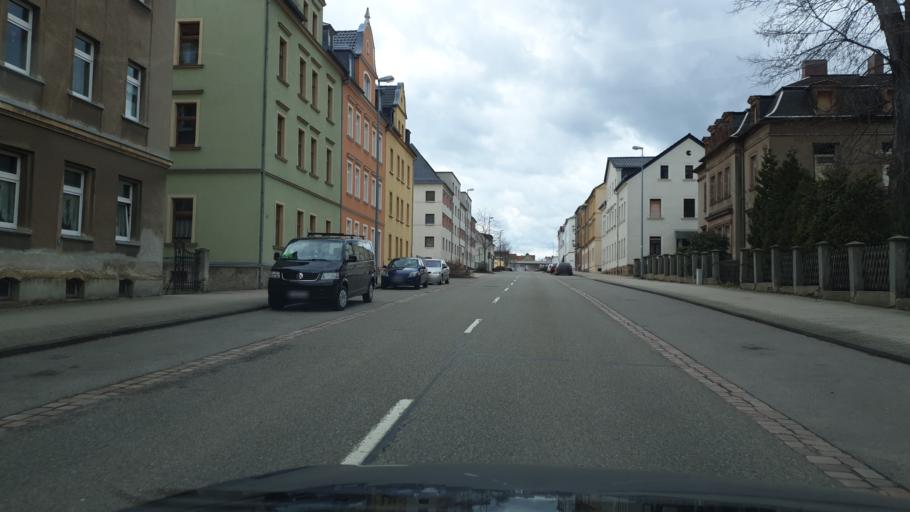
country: DE
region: Saxony
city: Mittweida
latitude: 50.9851
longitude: 12.9647
